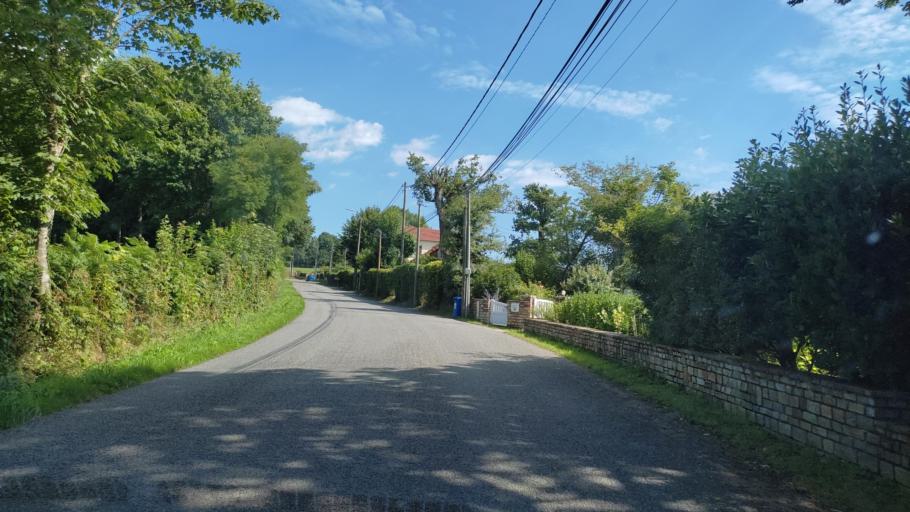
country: FR
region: Limousin
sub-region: Departement de la Haute-Vienne
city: Isle
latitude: 45.8469
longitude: 1.1922
